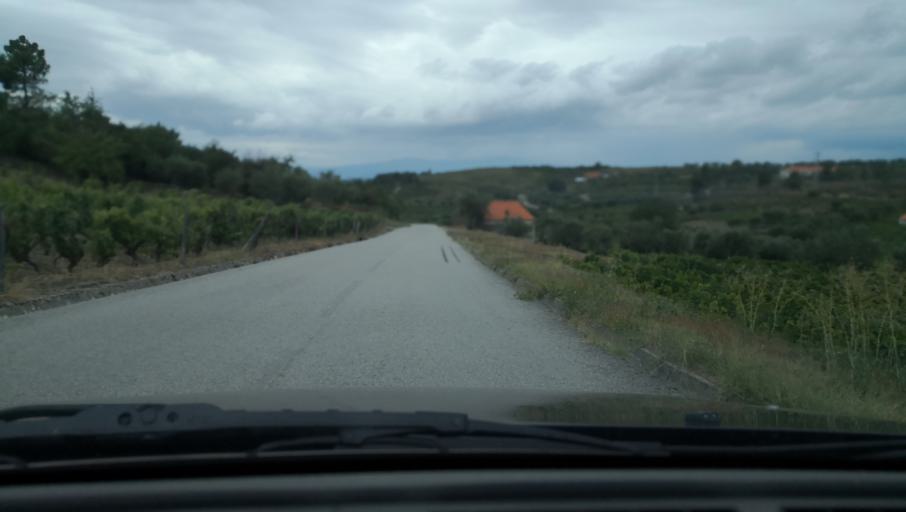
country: PT
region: Viseu
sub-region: Tabuaco
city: Tabuaco
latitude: 41.1255
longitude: -7.5914
